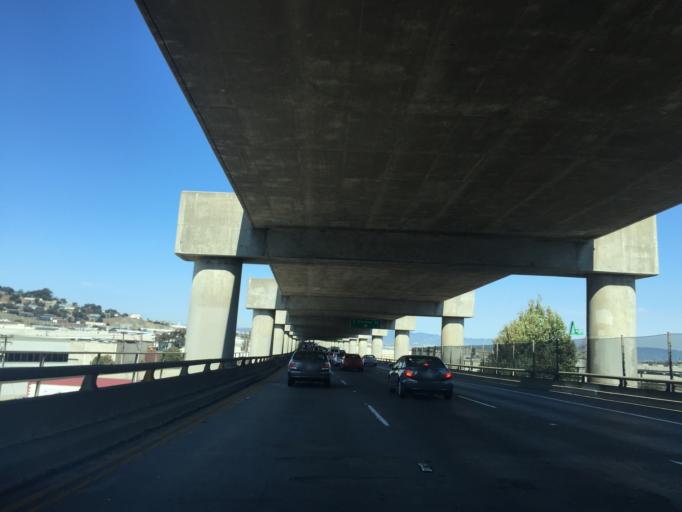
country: US
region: California
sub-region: San Francisco County
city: San Francisco
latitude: 37.7387
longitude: -122.4008
